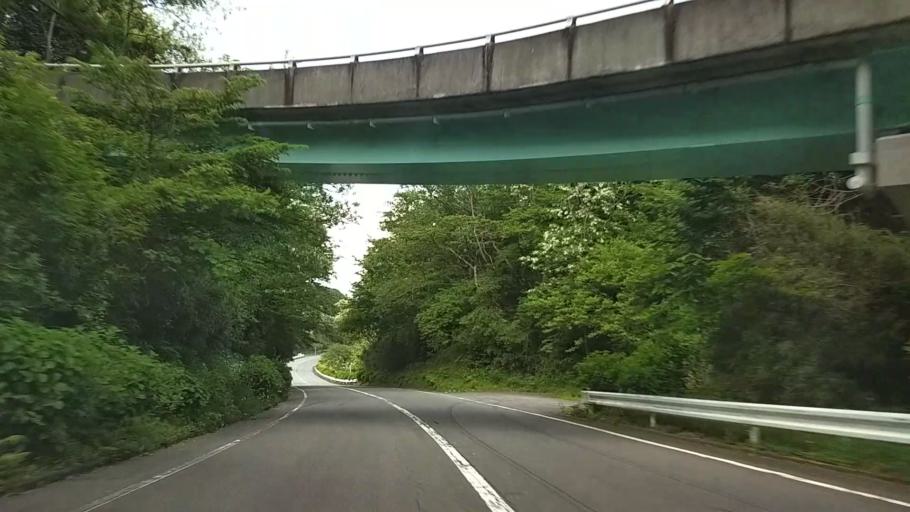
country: JP
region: Kanagawa
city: Odawara
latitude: 35.2224
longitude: 139.1147
